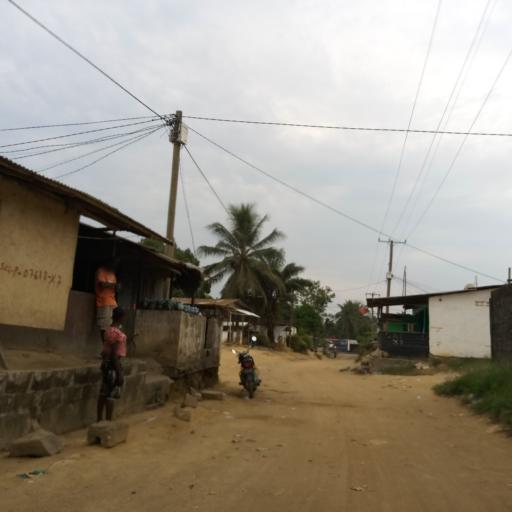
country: LR
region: Montserrado
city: Monrovia
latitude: 6.2956
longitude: -10.6816
